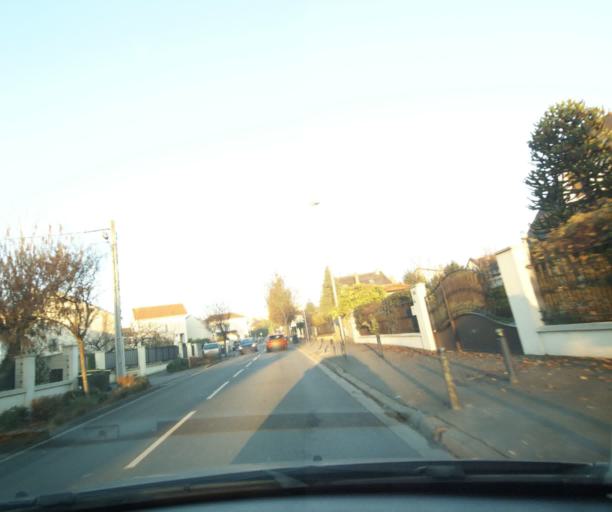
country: FR
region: Ile-de-France
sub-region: Departement de Seine-Saint-Denis
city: Gagny
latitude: 48.8749
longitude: 2.5274
